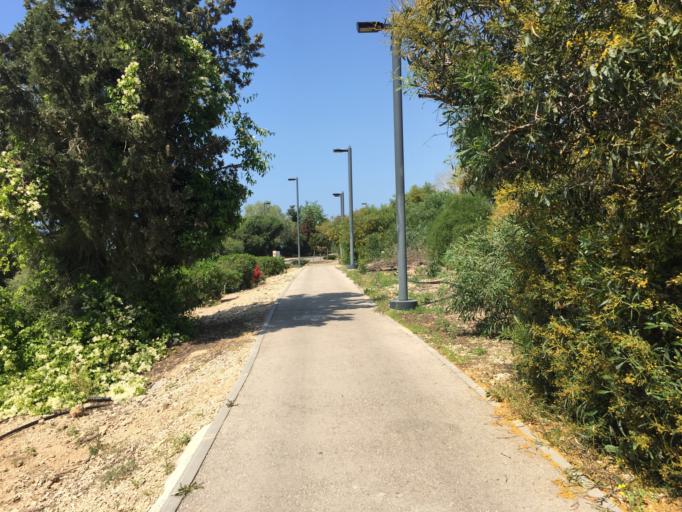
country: IL
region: Haifa
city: Qesarya
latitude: 32.4976
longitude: 34.9039
